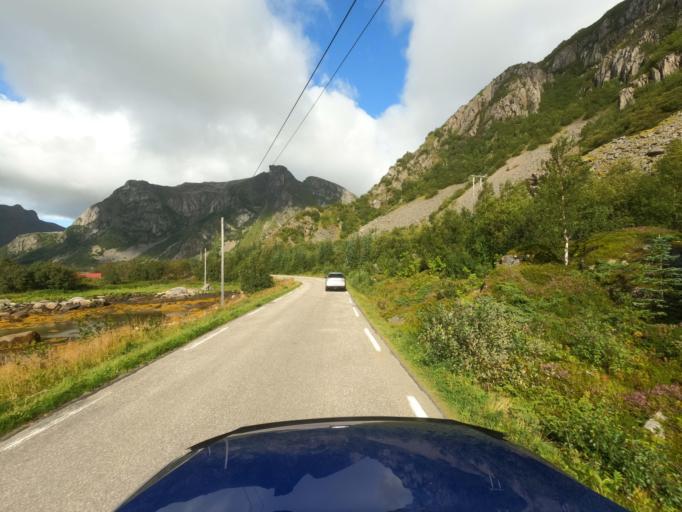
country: NO
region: Nordland
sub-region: Vestvagoy
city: Evjen
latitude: 68.1956
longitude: 14.0004
